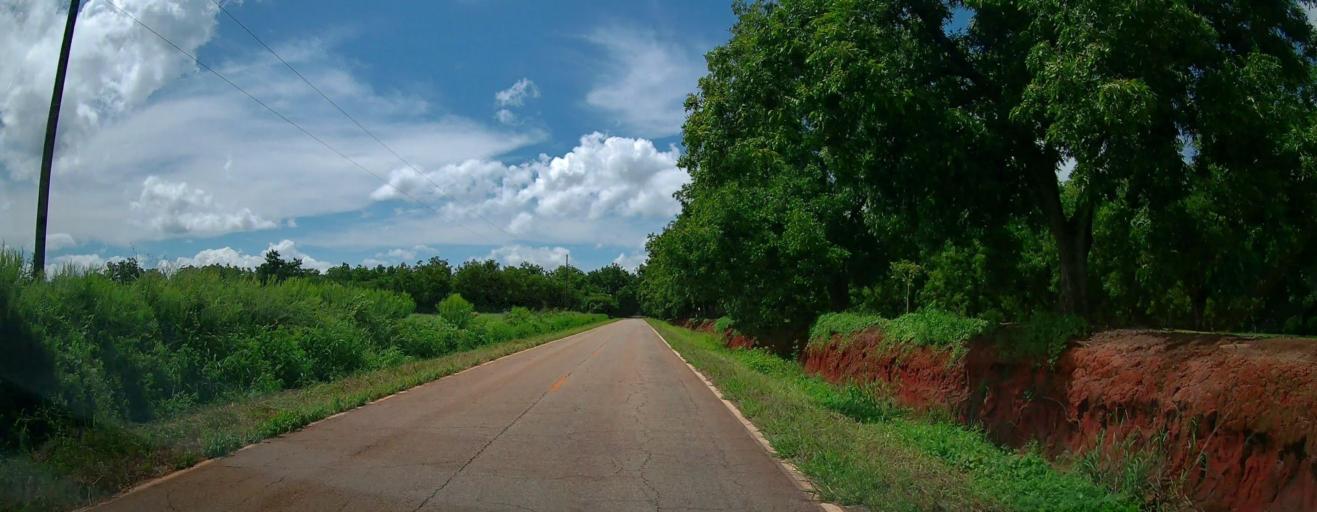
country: US
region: Georgia
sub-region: Houston County
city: Perry
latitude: 32.5212
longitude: -83.7841
